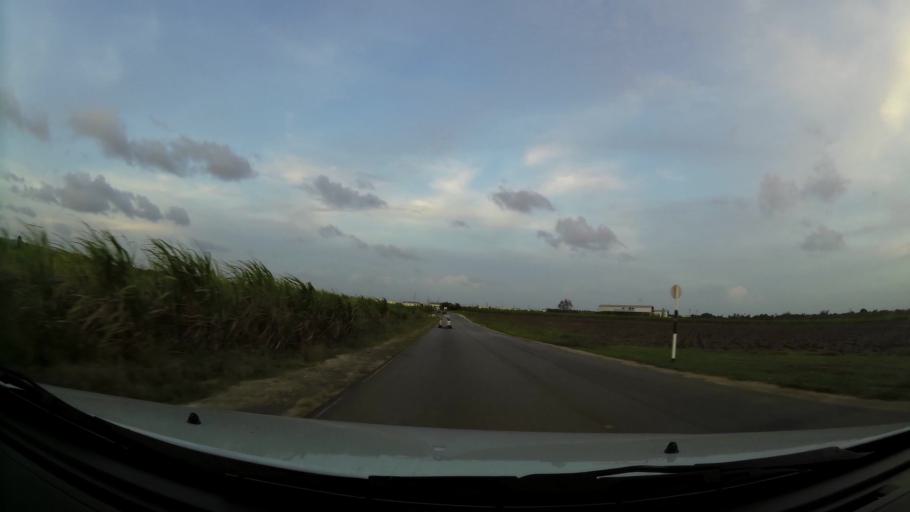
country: BB
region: Saint Philip
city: Crane
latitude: 13.1114
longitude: -59.4819
